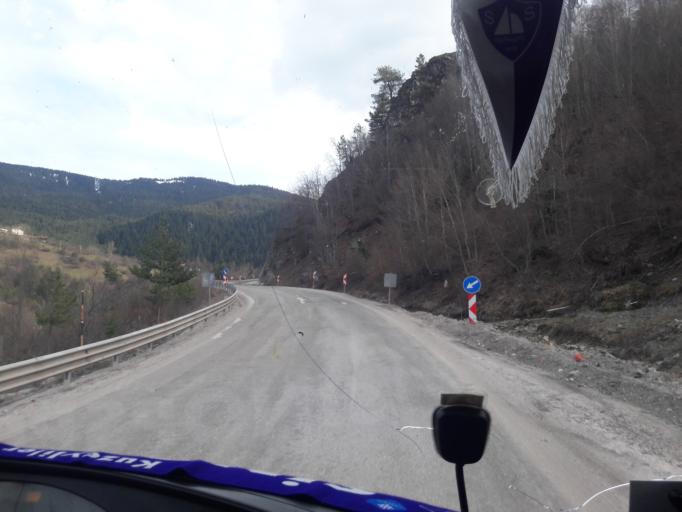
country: TR
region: Kastamonu
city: Kuzyaka
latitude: 41.1094
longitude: 33.7502
